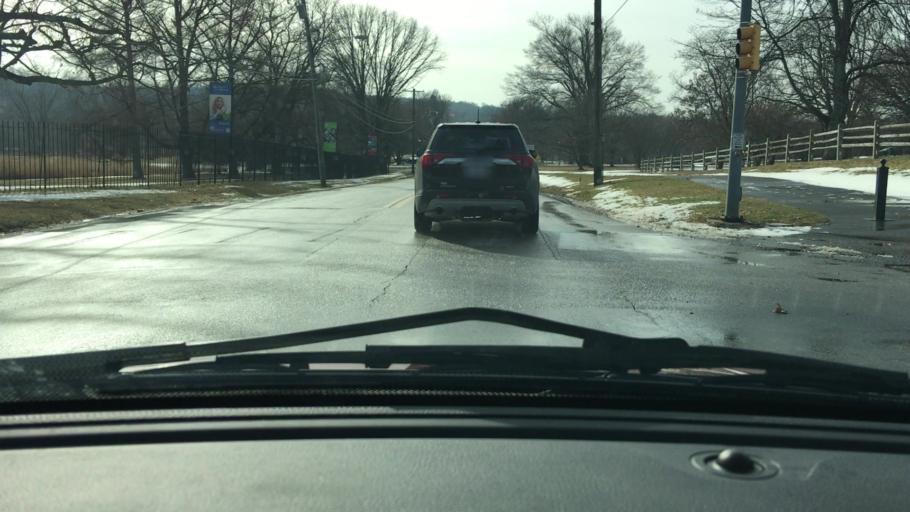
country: US
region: Pennsylvania
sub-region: Montgomery County
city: Flourtown
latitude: 40.0929
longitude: -75.2236
